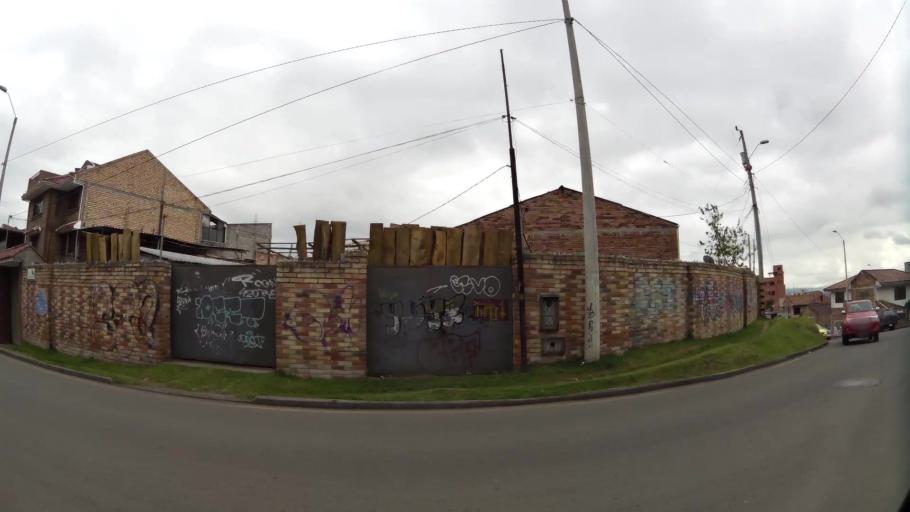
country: EC
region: Azuay
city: Cuenca
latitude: -2.9090
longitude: -79.0173
